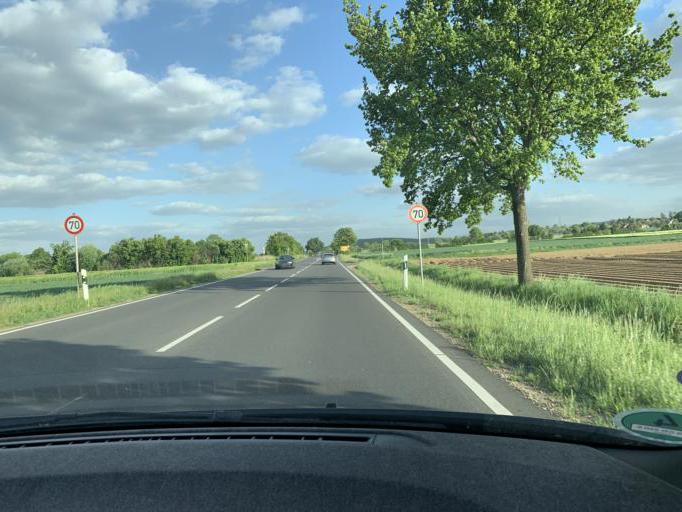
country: DE
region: North Rhine-Westphalia
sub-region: Regierungsbezirk Koln
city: Kreuzau
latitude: 50.7712
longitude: 6.4607
